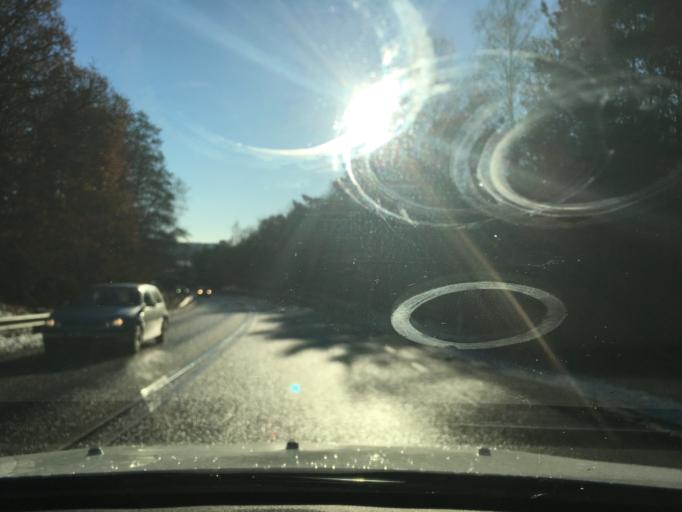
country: SE
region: Vaestra Goetaland
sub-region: Tjorns Kommun
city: Myggenas
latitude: 58.0818
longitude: 11.6945
